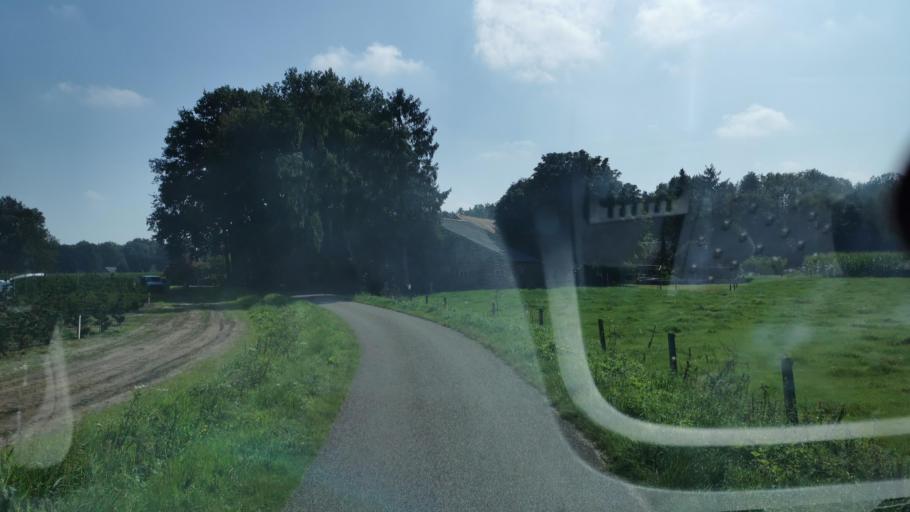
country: NL
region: Overijssel
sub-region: Gemeente Tubbergen
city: Tubbergen
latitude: 52.3503
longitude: 6.8442
